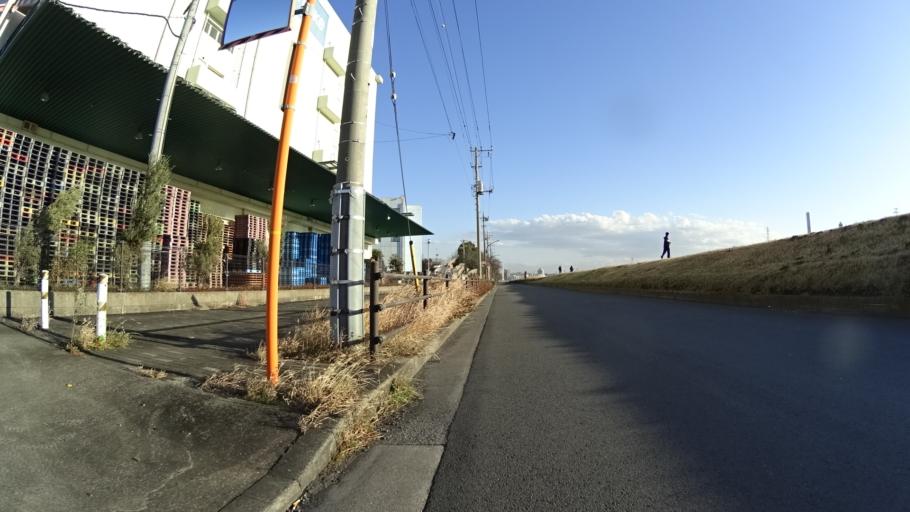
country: JP
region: Tokyo
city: Hino
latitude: 35.6722
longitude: 139.4300
